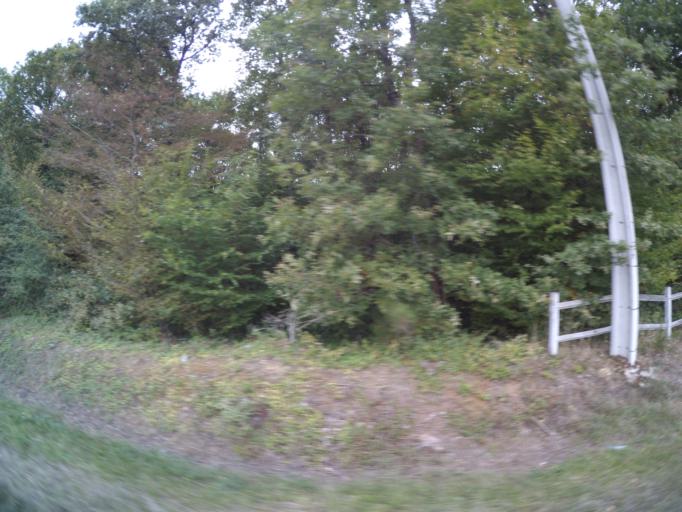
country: FR
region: Centre
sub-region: Departement d'Indre-et-Loire
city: Auzouer-en-Touraine
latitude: 47.5155
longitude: 0.9835
